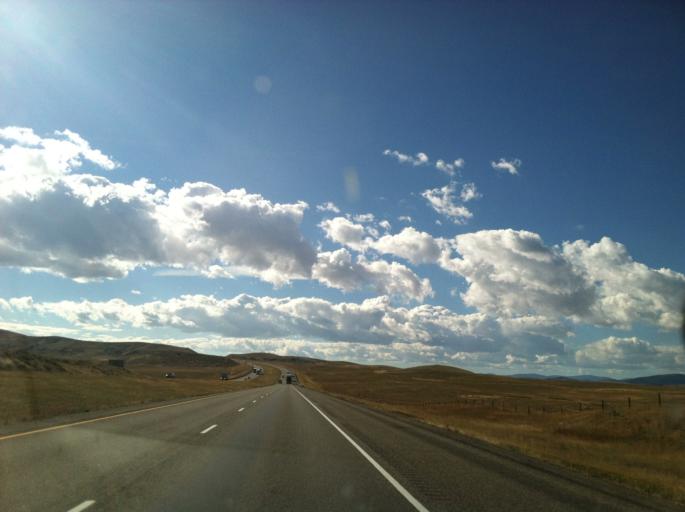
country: US
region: Montana
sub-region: Gallatin County
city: Three Forks
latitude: 45.9201
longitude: -111.6431
